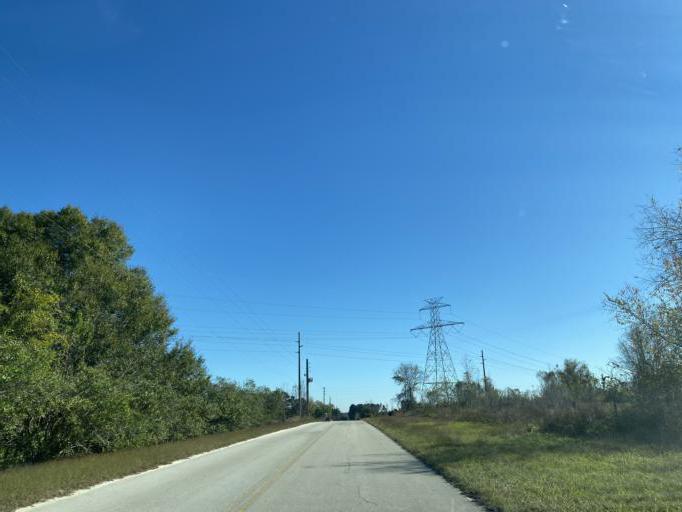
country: US
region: Florida
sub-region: Orange County
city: Oakland
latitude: 28.5251
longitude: -81.6923
